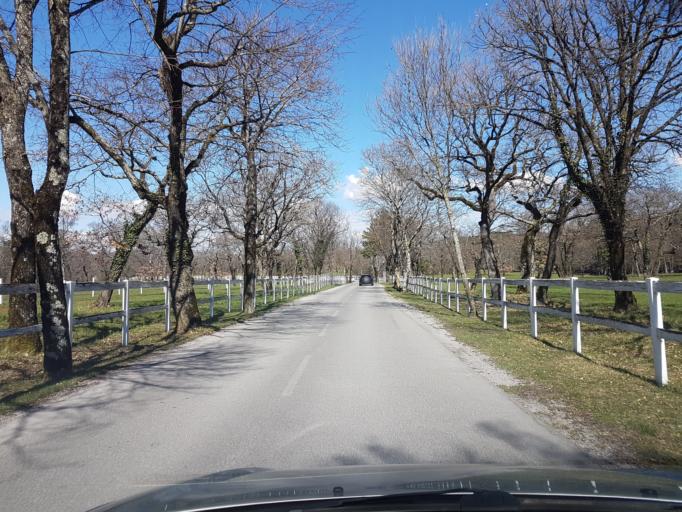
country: SI
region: Sezana
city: Sezana
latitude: 45.6616
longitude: 13.8899
